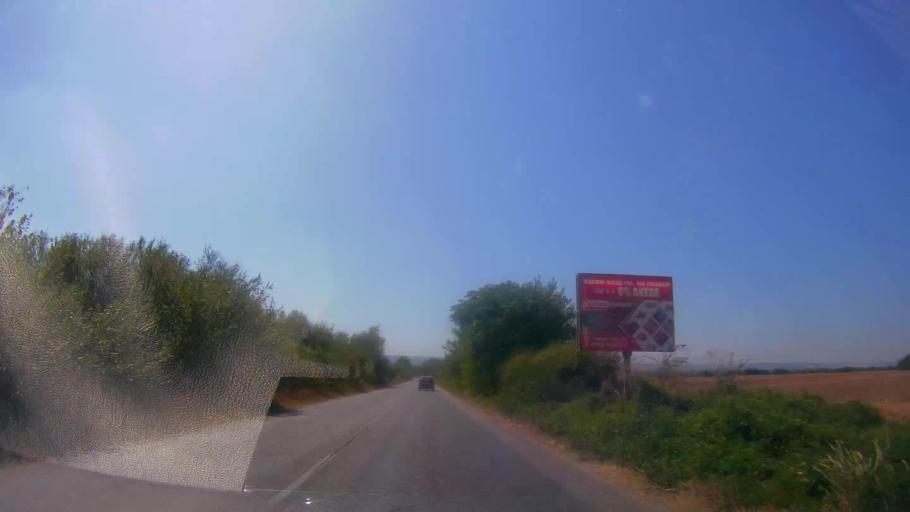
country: BG
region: Veliko Turnovo
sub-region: Obshtina Gorna Oryakhovitsa
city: Purvomaytsi
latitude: 43.2240
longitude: 25.6374
